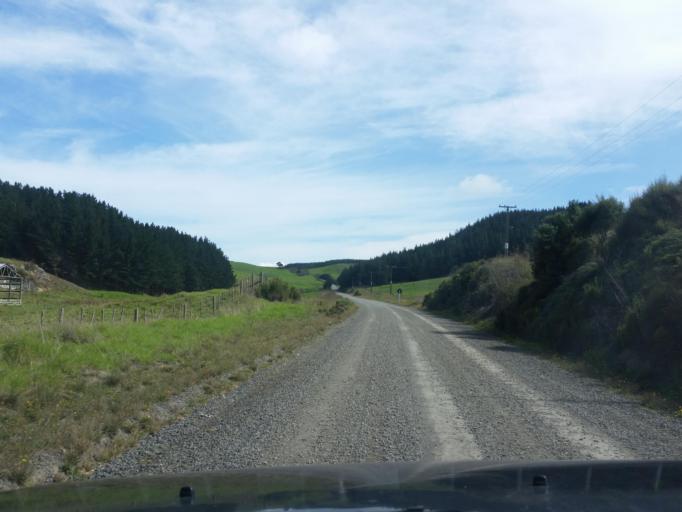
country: NZ
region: Northland
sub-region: Kaipara District
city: Dargaville
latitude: -35.9350
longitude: 173.7703
